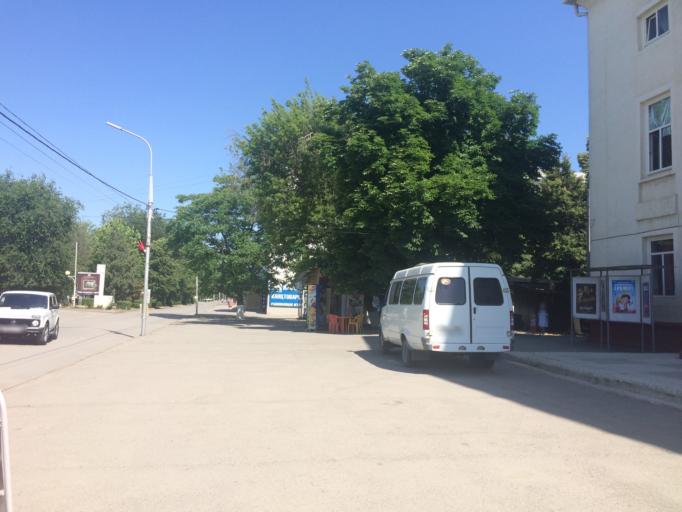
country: RU
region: Rostov
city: Sal'sk
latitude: 46.4725
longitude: 41.5444
